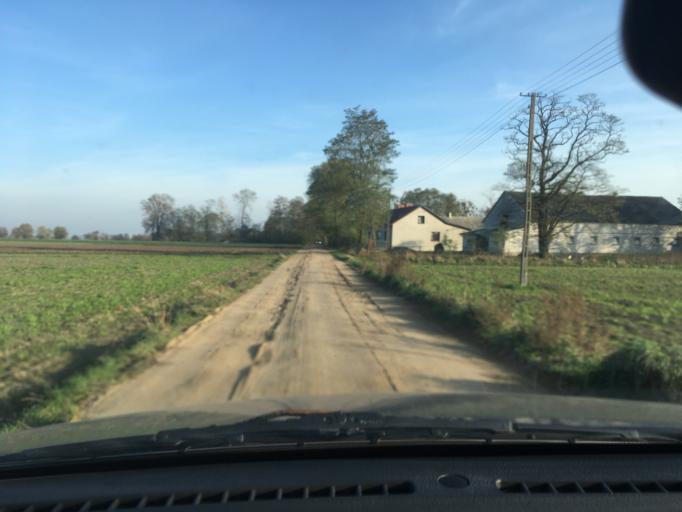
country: PL
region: Masovian Voivodeship
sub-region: Powiat plocki
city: Mala Wies
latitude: 52.4427
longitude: 20.1097
